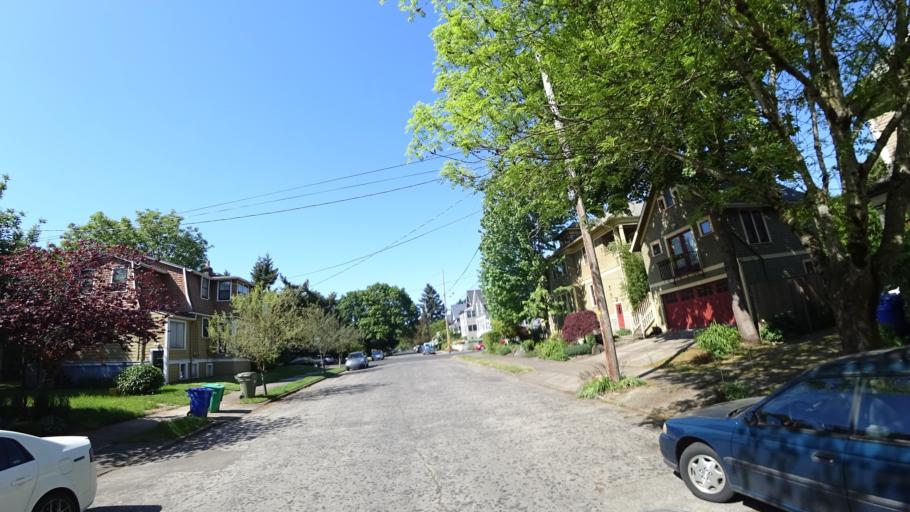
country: US
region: Oregon
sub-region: Multnomah County
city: Portland
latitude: 45.5370
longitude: -122.6525
